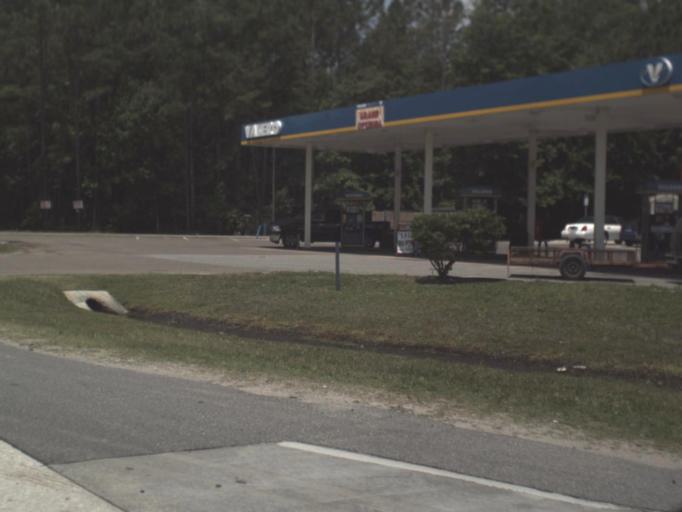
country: US
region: Florida
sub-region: Duval County
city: Baldwin
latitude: 30.2183
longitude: -81.9409
